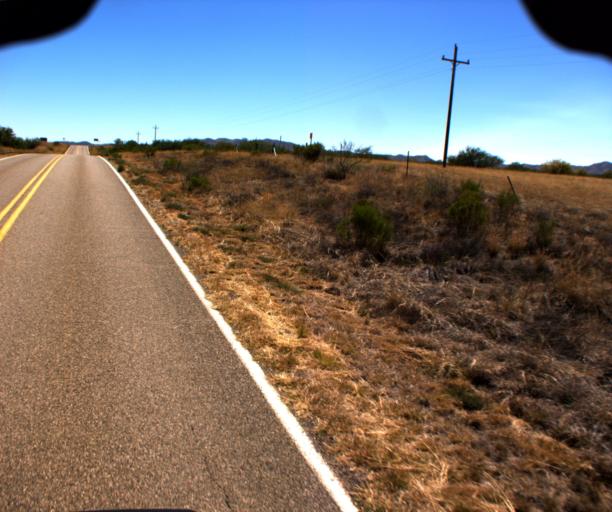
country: US
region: Arizona
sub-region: Pima County
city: Sells
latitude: 31.5918
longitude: -111.5299
